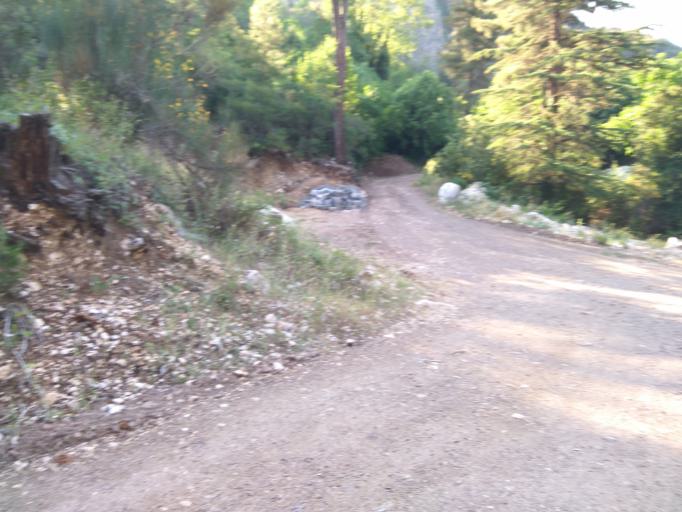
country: TR
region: Antalya
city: Altinyaka
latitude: 36.5726
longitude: 30.4198
